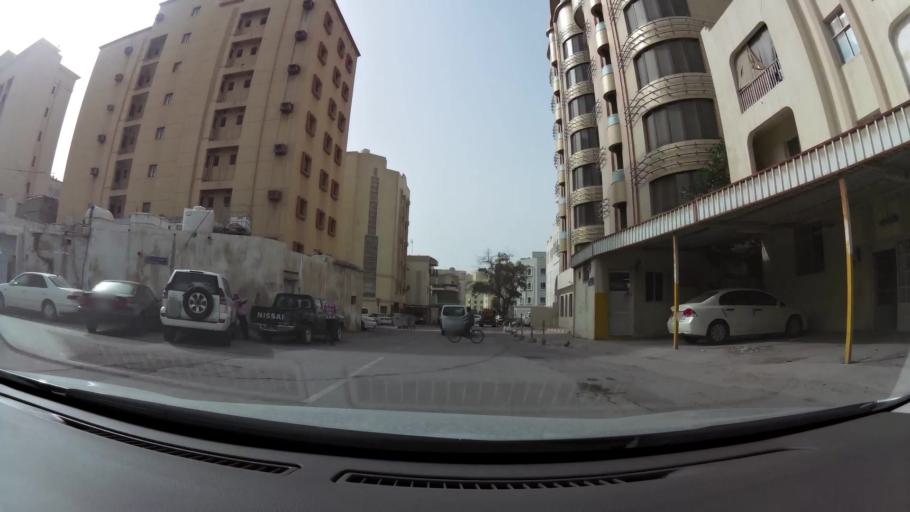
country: QA
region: Baladiyat ad Dawhah
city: Doha
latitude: 25.2784
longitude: 51.5498
